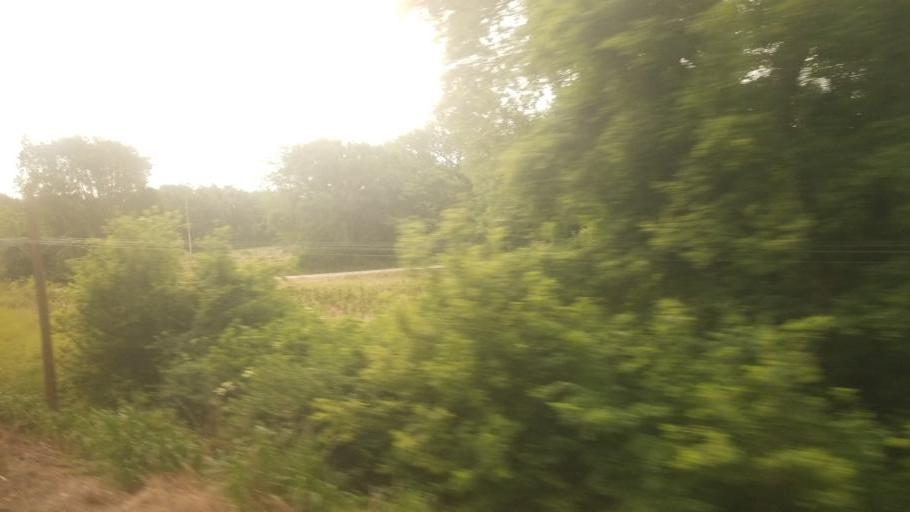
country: US
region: Kansas
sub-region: Shawnee County
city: Topeka
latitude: 39.0596
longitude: -95.5540
